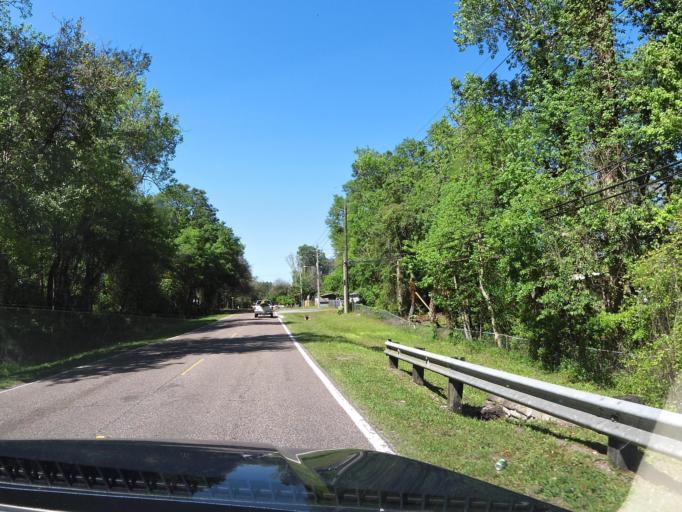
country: US
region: Florida
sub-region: Duval County
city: Jacksonville
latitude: 30.4519
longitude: -81.6014
